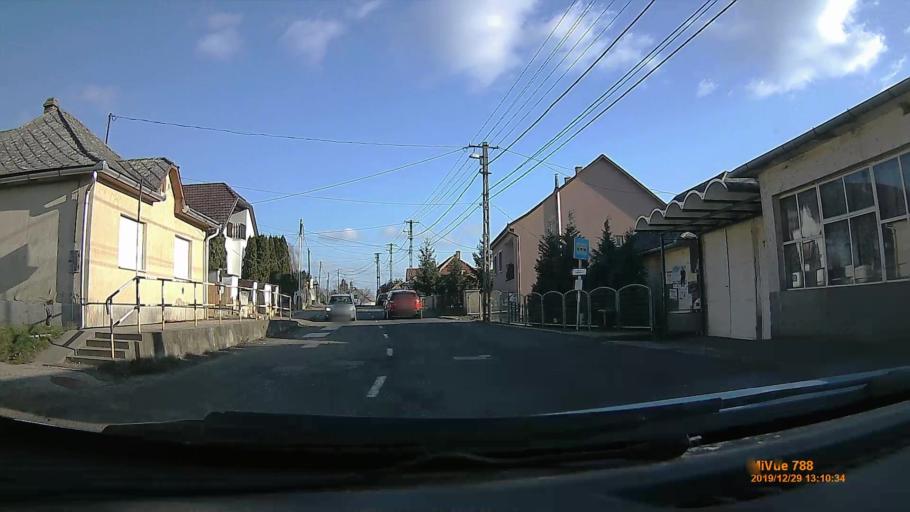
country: HU
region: Heves
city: Domoszlo
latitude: 47.8267
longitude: 20.0578
